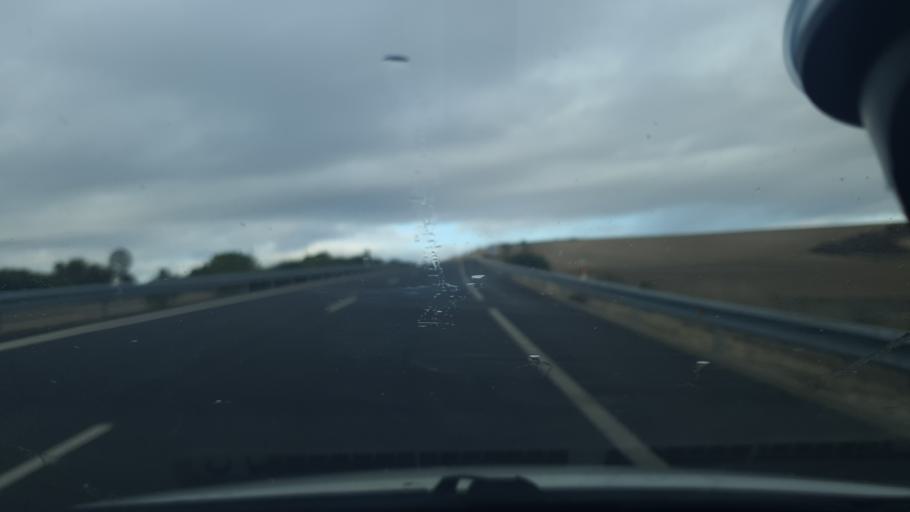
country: ES
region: Castille and Leon
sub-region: Provincia de Segovia
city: Cuellar
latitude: 41.3995
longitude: -4.2931
